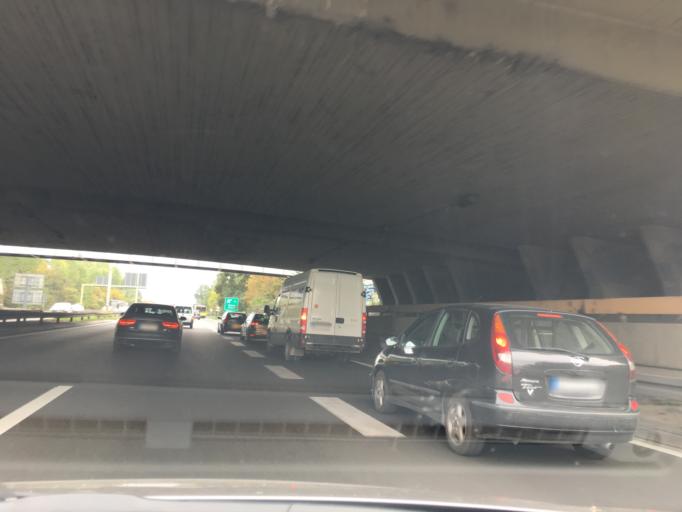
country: RS
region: Central Serbia
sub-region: Belgrade
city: Novi Beograd
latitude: 44.8163
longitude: 20.4116
